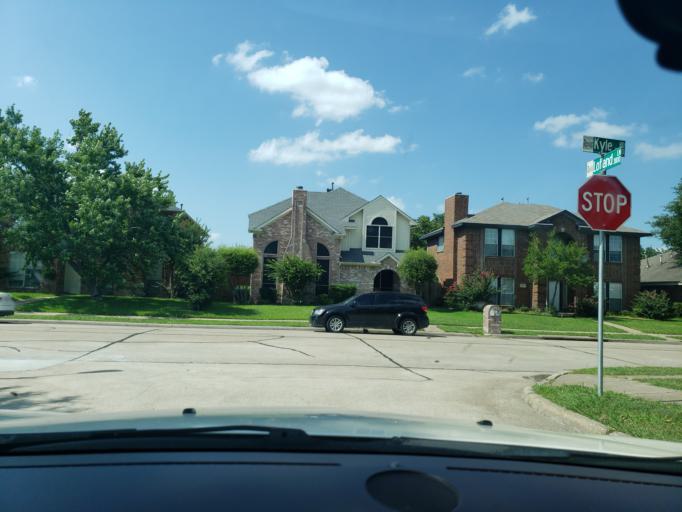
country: US
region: Texas
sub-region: Dallas County
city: Rowlett
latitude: 32.8967
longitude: -96.5751
